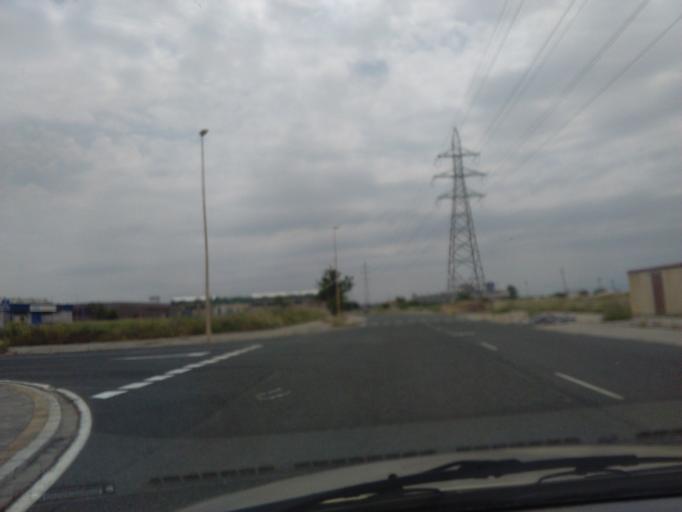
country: ES
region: Andalusia
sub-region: Provincia de Sevilla
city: Sevilla
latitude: 37.3839
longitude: -5.9339
